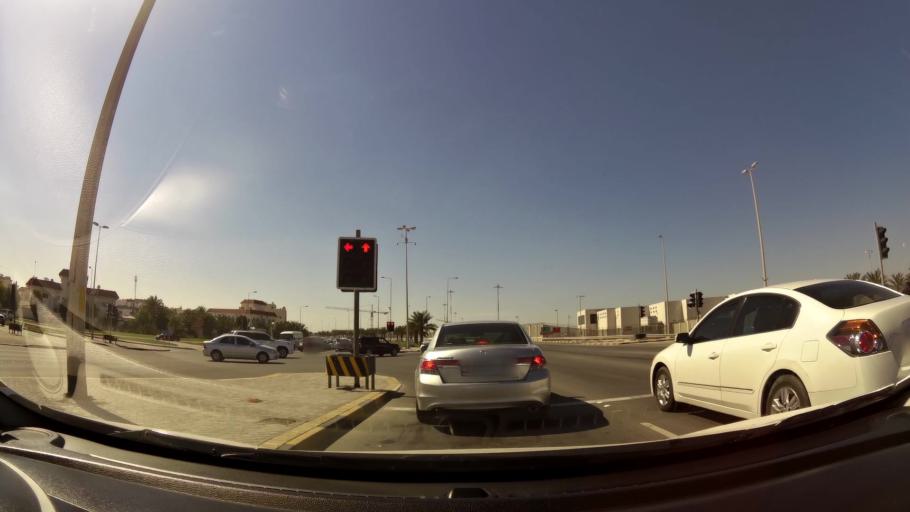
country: BH
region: Muharraq
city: Al Hadd
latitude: 26.2619
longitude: 50.6411
